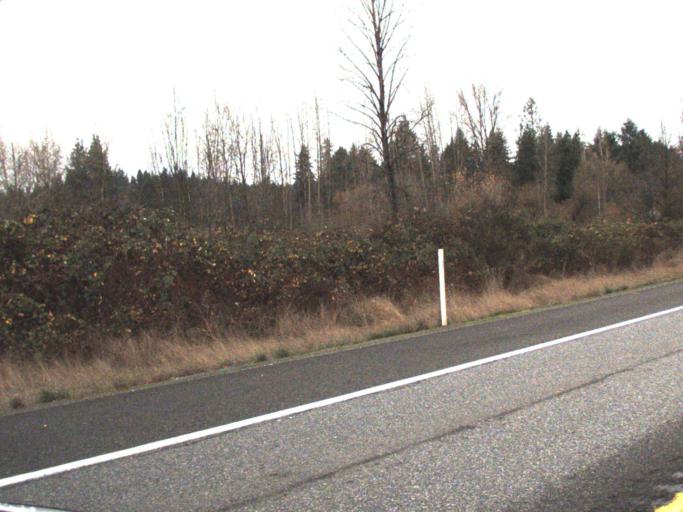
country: US
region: Washington
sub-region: Snohomish County
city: Snohomish
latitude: 47.9270
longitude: -122.1081
